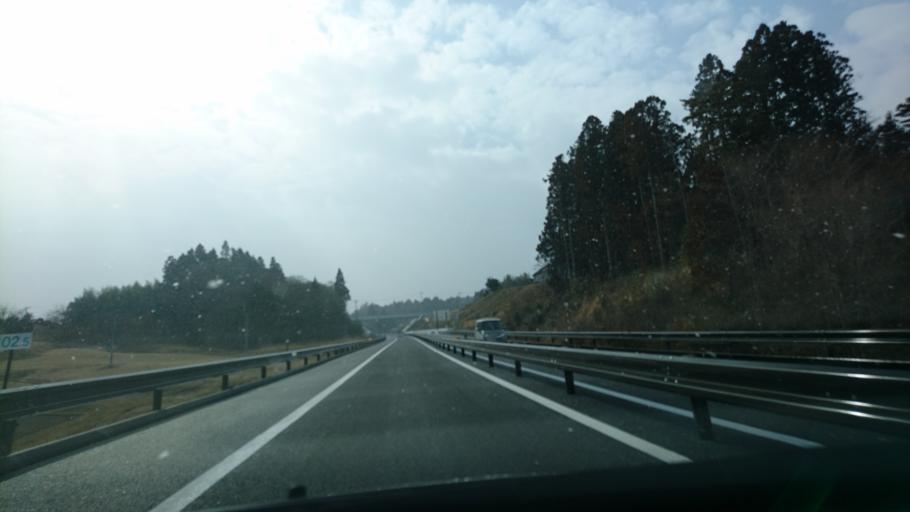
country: JP
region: Iwate
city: Ofunato
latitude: 38.8007
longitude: 141.5345
